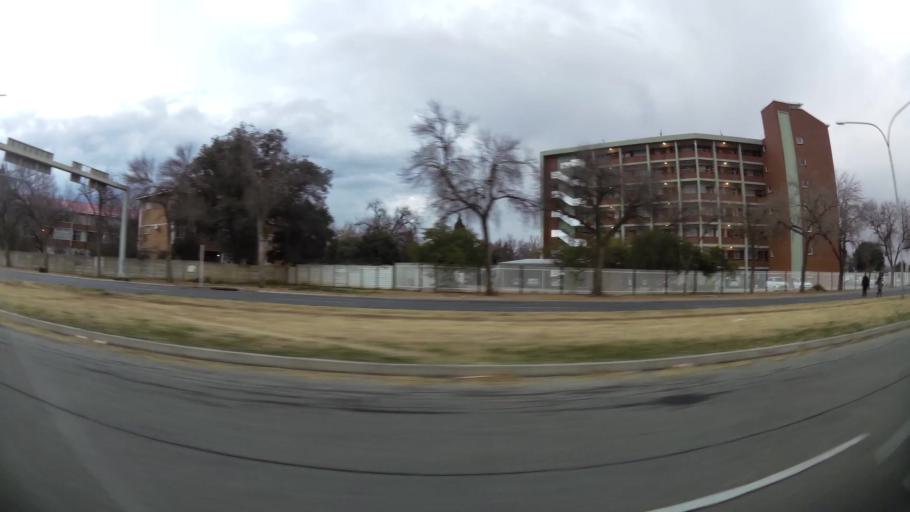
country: ZA
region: Orange Free State
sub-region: Lejweleputswa District Municipality
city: Welkom
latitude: -27.9654
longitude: 26.7484
